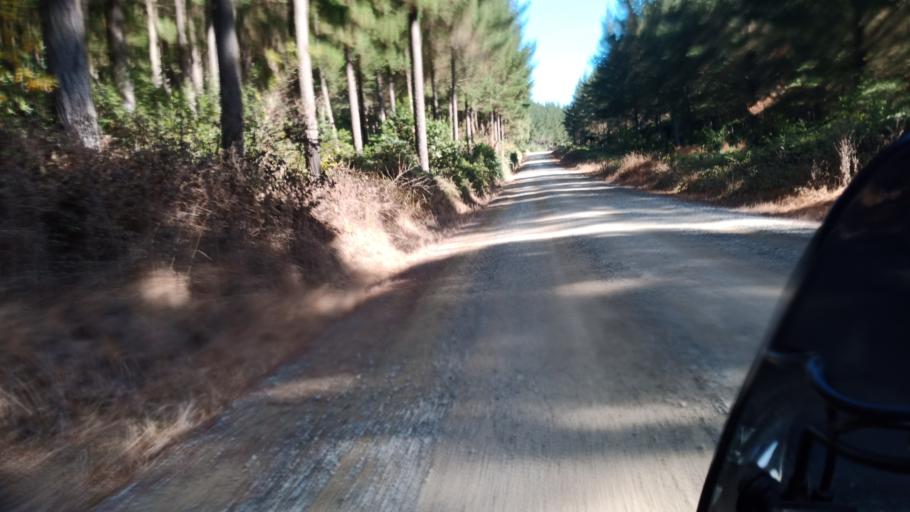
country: NZ
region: Hawke's Bay
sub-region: Wairoa District
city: Wairoa
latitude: -38.9239
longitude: 177.2103
